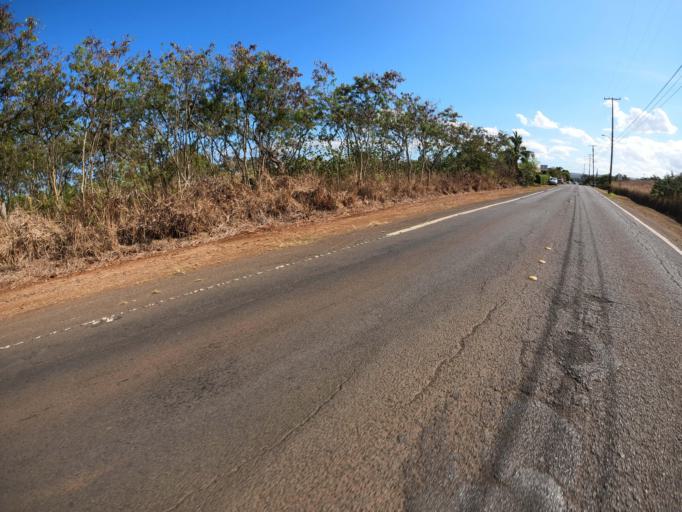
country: US
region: Hawaii
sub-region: Honolulu County
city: Waialua
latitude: 21.5692
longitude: -158.1345
